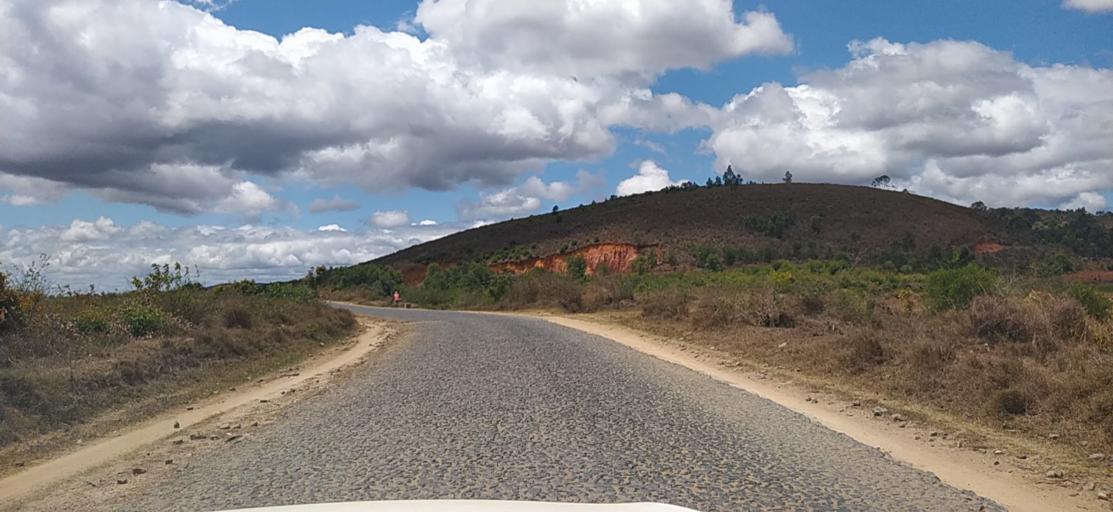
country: MG
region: Alaotra Mangoro
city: Moramanga
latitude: -18.7587
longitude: 48.2582
